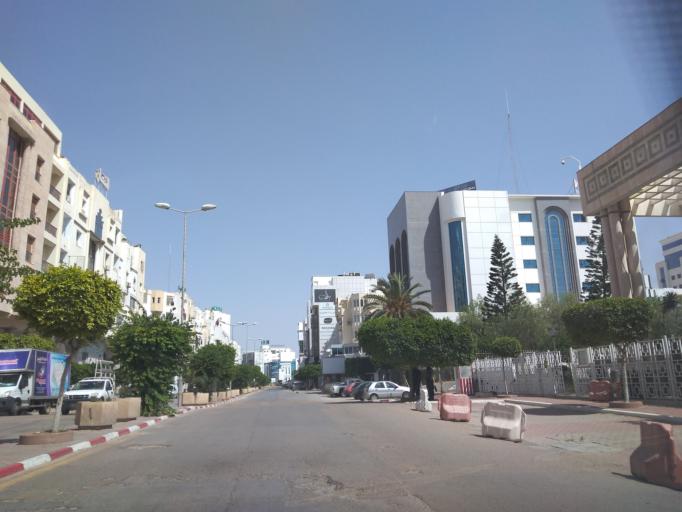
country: TN
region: Safaqis
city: Sfax
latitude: 34.7388
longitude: 10.7545
